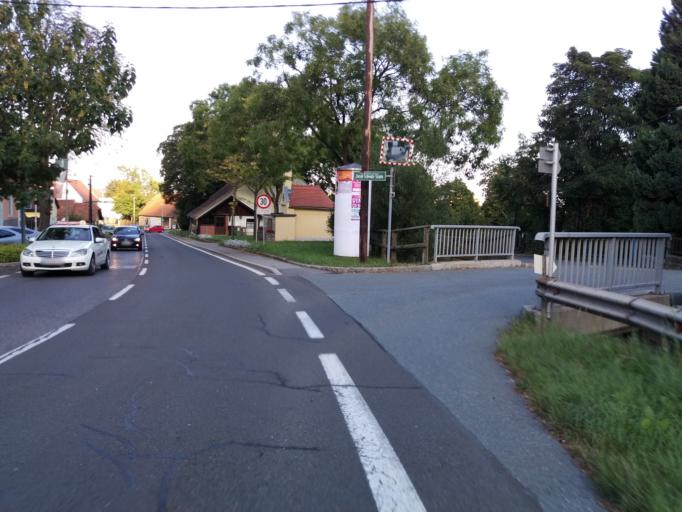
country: AT
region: Styria
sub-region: Graz Stadt
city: Wetzelsdorf
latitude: 47.0583
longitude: 15.3877
